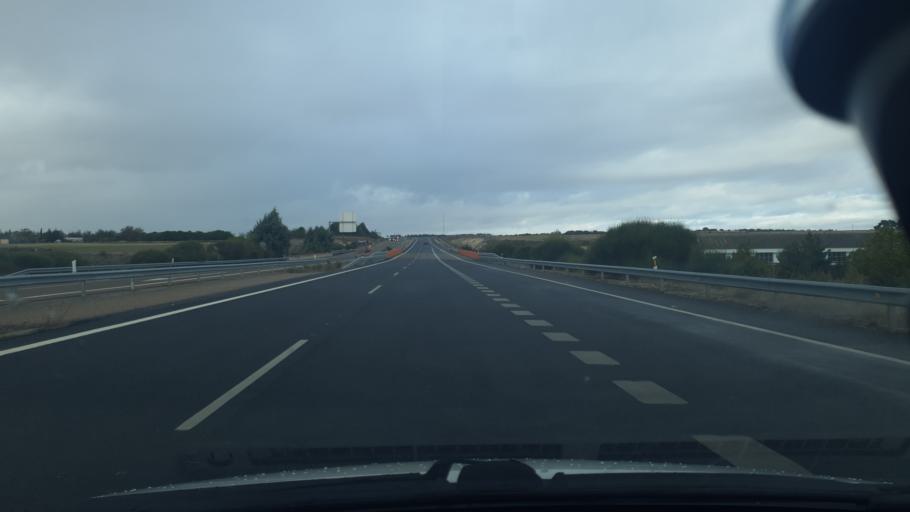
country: ES
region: Castille and Leon
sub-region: Provincia de Segovia
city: Cuellar
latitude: 41.4067
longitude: -4.2962
